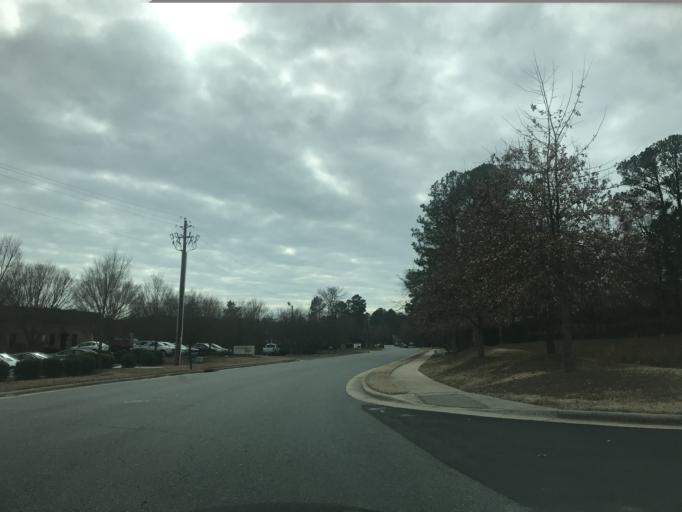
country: US
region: North Carolina
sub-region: Wake County
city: Raleigh
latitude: 35.8799
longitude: -78.5907
